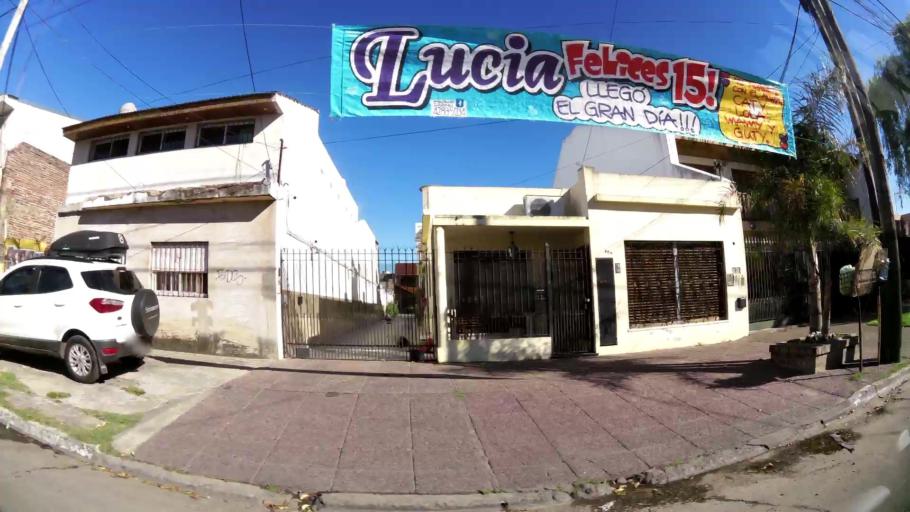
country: AR
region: Buenos Aires
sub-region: Partido de Lomas de Zamora
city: Lomas de Zamora
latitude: -34.7715
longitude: -58.4162
